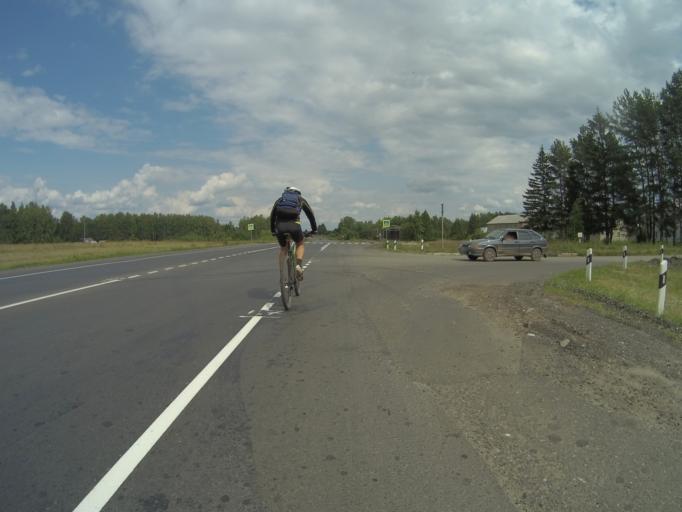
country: RU
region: Vladimir
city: Kideksha
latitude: 56.4984
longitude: 40.5334
